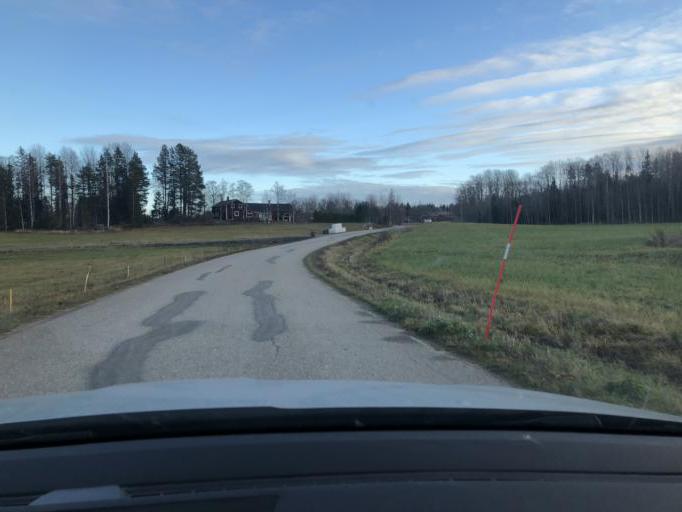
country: SE
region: Gaevleborg
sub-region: Hudiksvalls Kommun
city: Sorforsa
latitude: 61.7194
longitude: 16.9244
